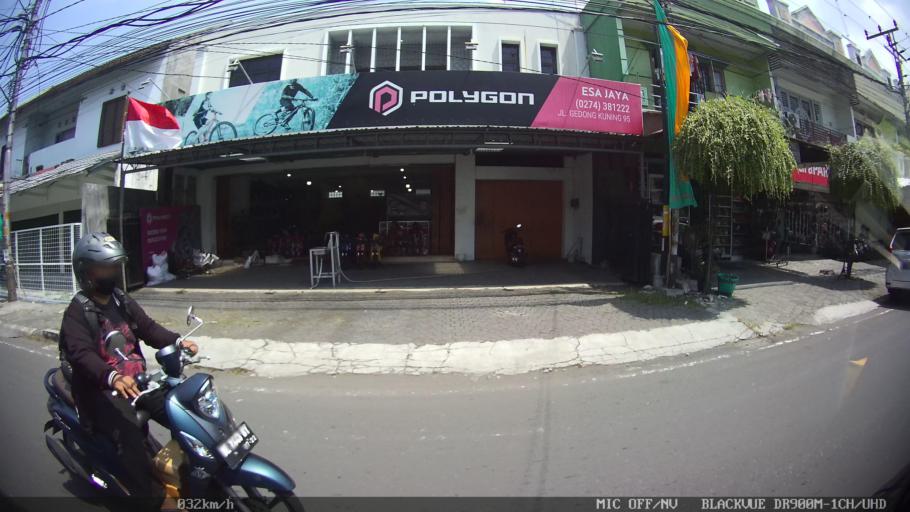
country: ID
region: Daerah Istimewa Yogyakarta
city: Yogyakarta
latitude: -7.8102
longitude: 110.4021
